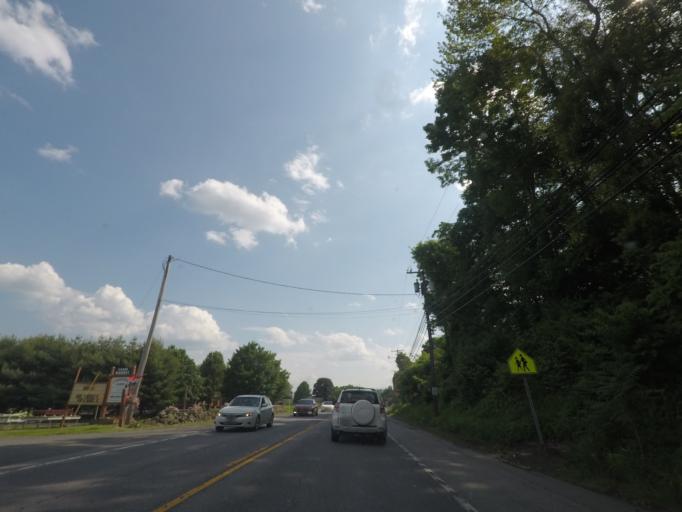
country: US
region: New York
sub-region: Ulster County
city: Marlboro
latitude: 41.6109
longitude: -73.9676
